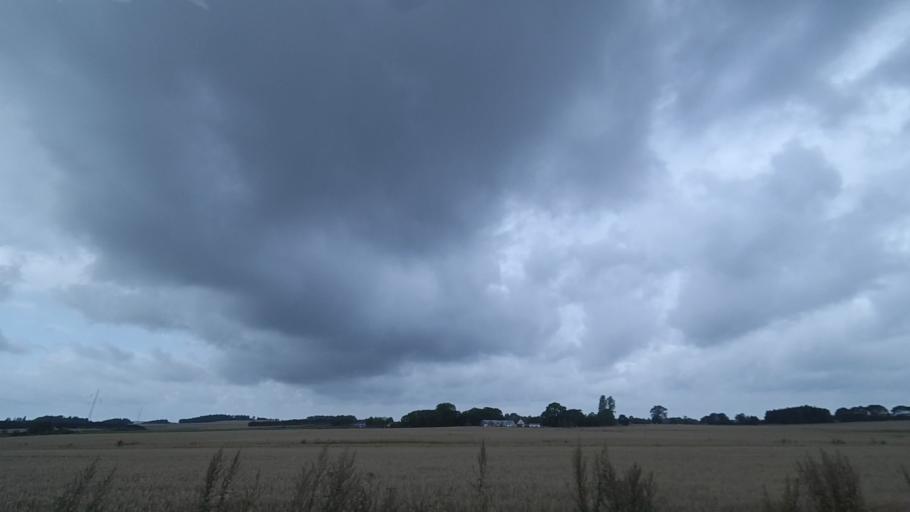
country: DK
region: Central Jutland
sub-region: Syddjurs Kommune
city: Ryomgard
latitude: 56.3887
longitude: 10.5661
